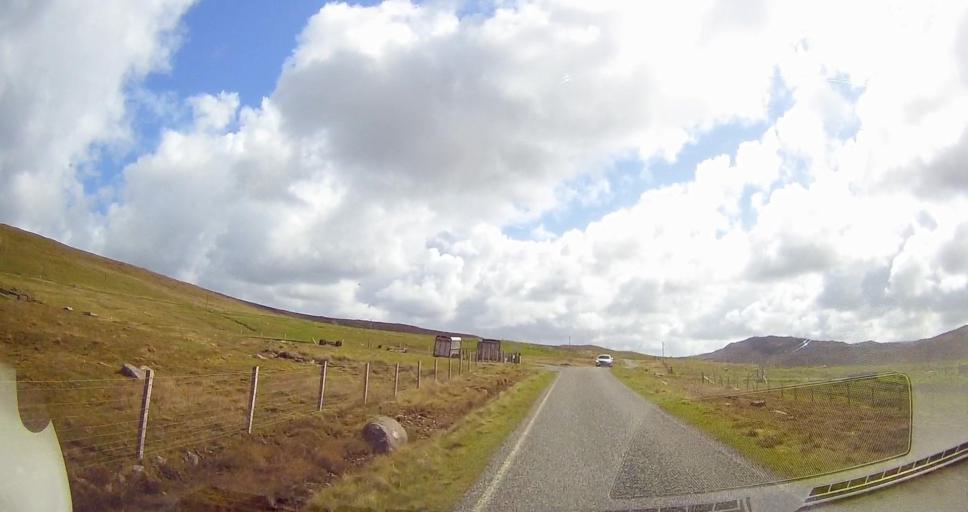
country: GB
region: Scotland
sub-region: Shetland Islands
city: Lerwick
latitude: 60.5673
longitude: -1.3330
